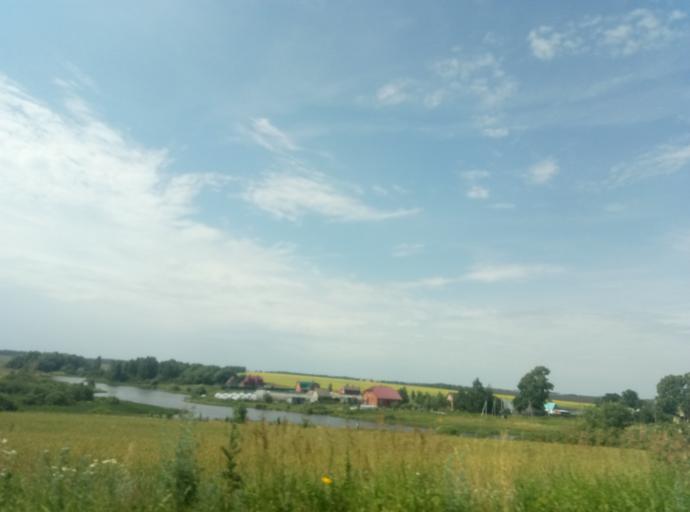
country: RU
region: Tula
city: Kireyevsk
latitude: 53.9038
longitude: 37.9791
